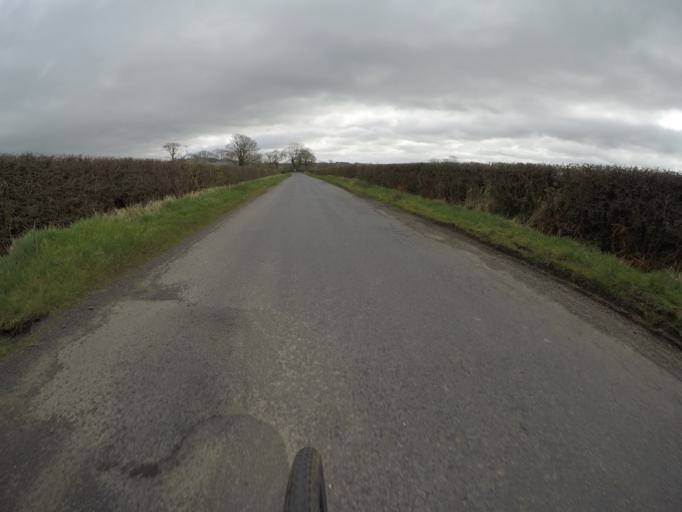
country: GB
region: Scotland
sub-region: East Ayrshire
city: Stewarton
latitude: 55.6721
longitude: -4.5594
